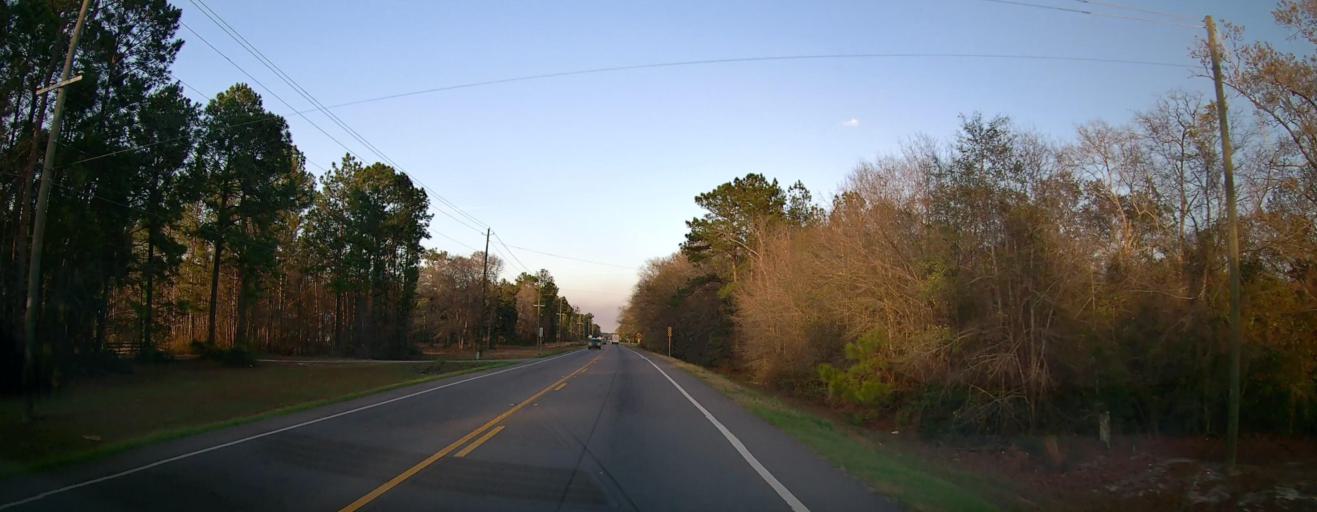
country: US
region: Georgia
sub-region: Chatham County
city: Bloomingdale
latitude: 32.1852
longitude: -81.4528
